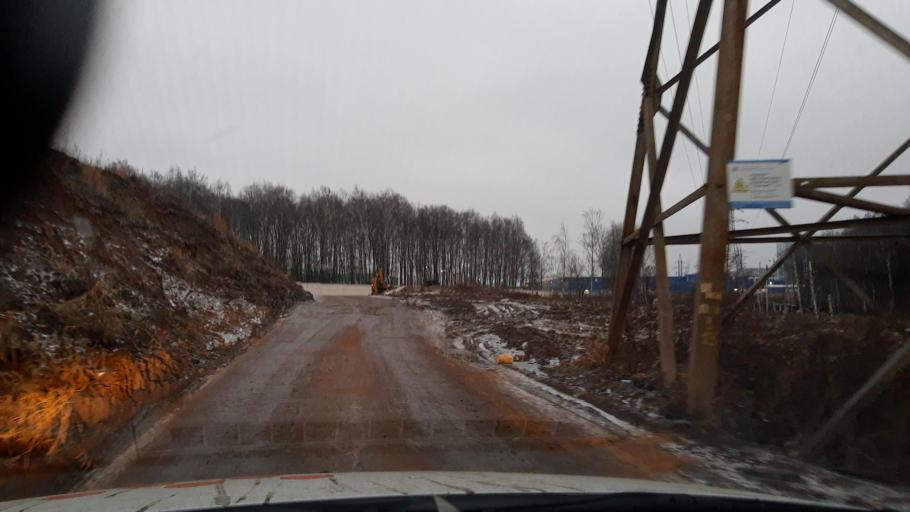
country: RU
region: Moscow
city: Solntsevo
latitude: 55.6235
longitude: 37.3853
